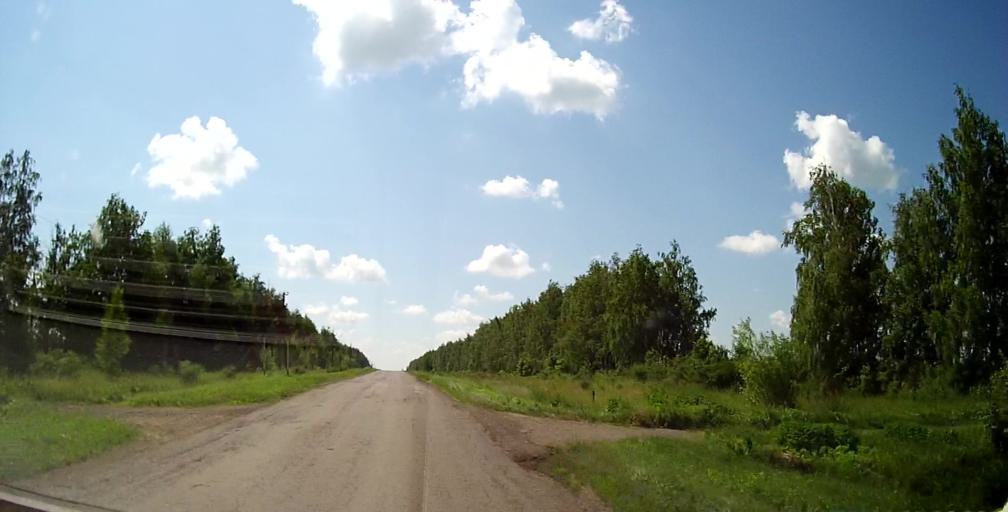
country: RU
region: Lipetsk
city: Chaplygin
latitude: 53.3676
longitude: 39.9166
